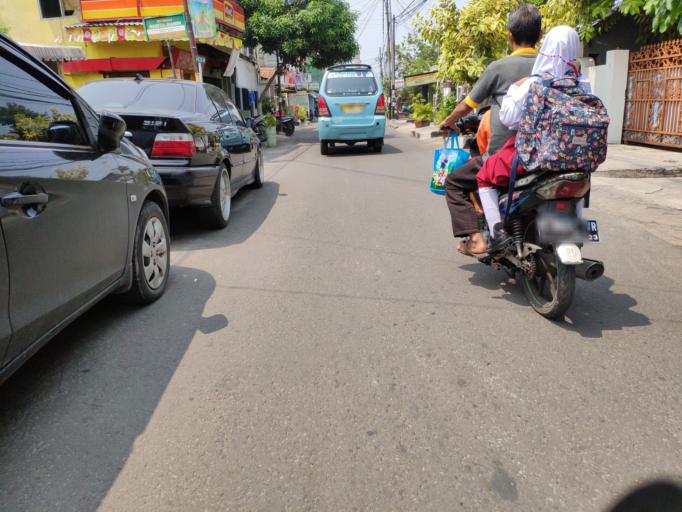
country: ID
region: Jakarta Raya
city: Jakarta
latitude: -6.2002
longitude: 106.8628
